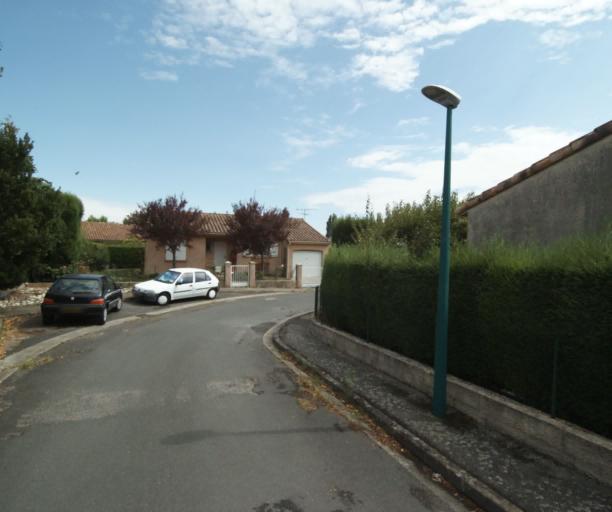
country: FR
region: Midi-Pyrenees
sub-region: Departement de la Haute-Garonne
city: Revel
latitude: 43.4622
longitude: 2.0028
